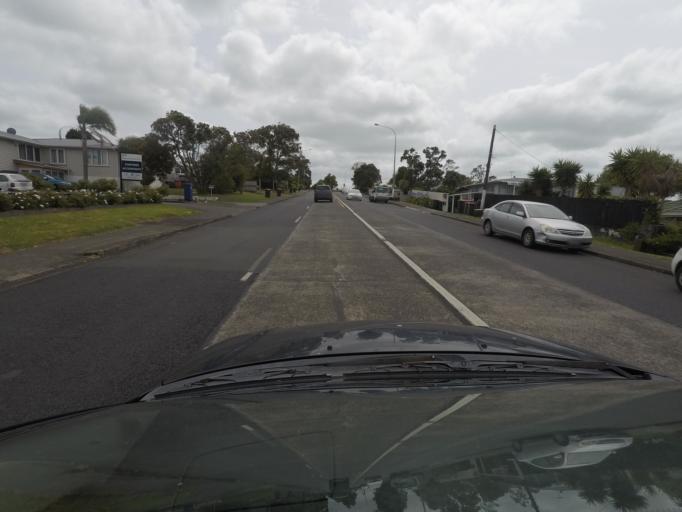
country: NZ
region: Auckland
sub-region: Auckland
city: Pakuranga
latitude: -36.8942
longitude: 174.9234
